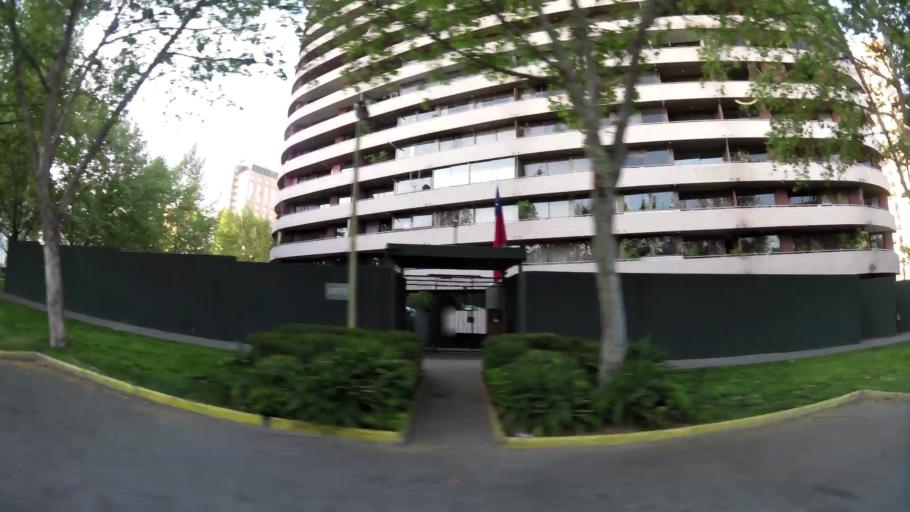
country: CL
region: Santiago Metropolitan
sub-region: Provincia de Santiago
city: Villa Presidente Frei, Nunoa, Santiago, Chile
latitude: -33.4054
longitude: -70.5773
